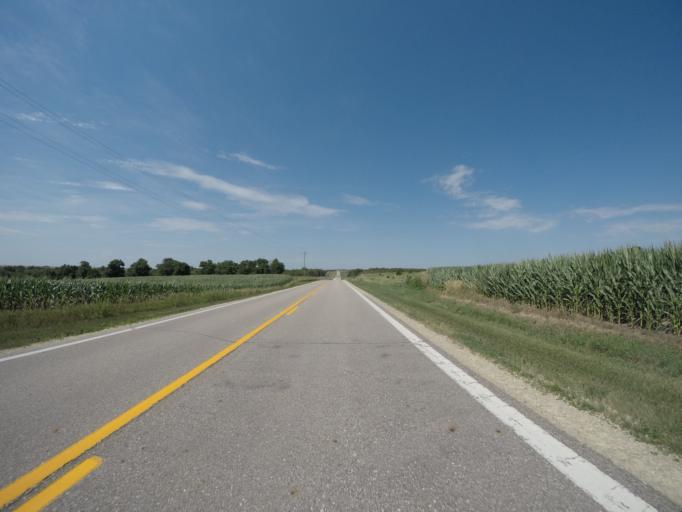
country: US
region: Kansas
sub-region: Jewell County
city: Mankato
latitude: 39.7910
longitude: -98.3062
